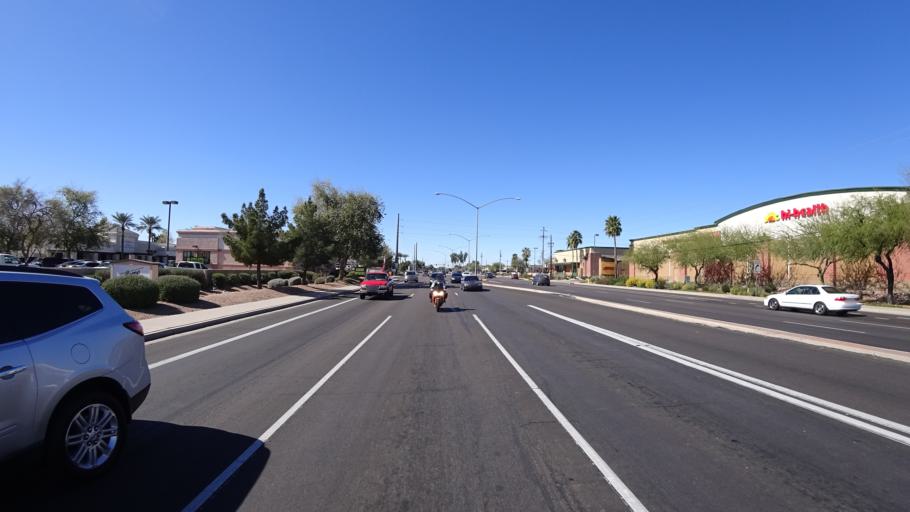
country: US
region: Arizona
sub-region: Maricopa County
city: Gilbert
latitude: 33.3789
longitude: -111.8044
